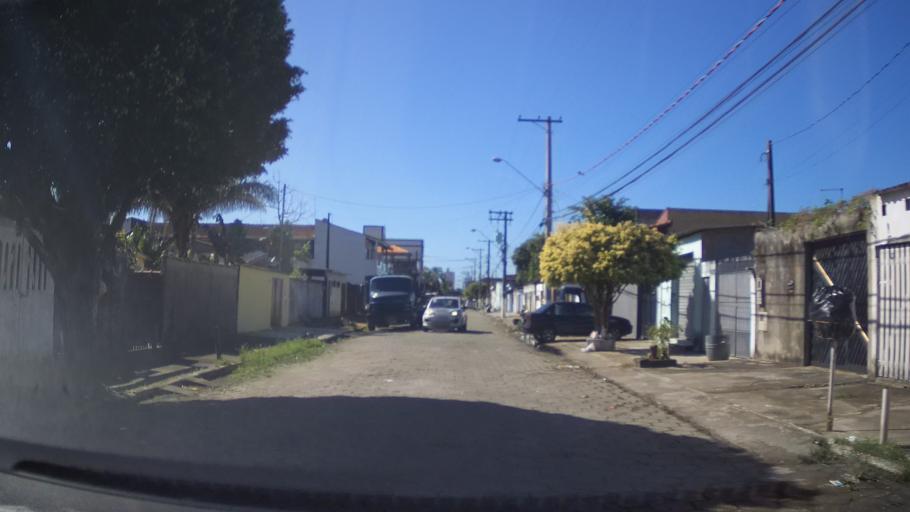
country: BR
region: Sao Paulo
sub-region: Praia Grande
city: Praia Grande
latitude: -24.0306
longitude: -46.5144
